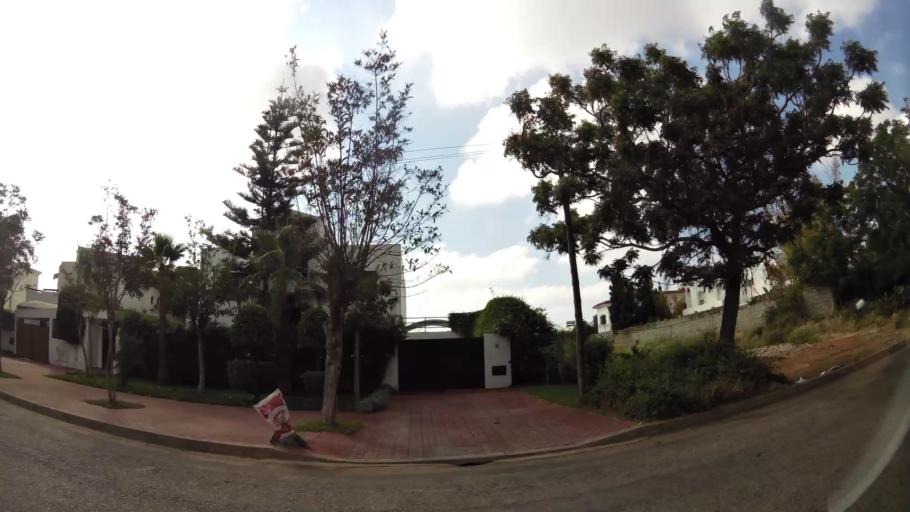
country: MA
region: Rabat-Sale-Zemmour-Zaer
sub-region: Skhirate-Temara
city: Temara
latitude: 33.9515
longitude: -6.8712
